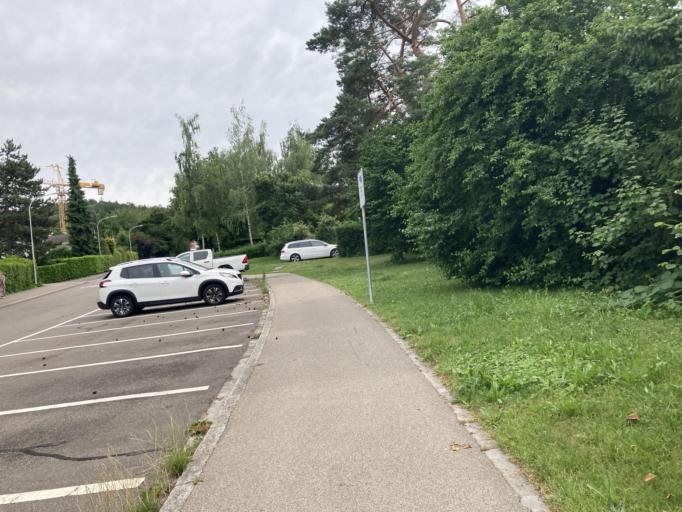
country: CH
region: Zurich
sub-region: Bezirk Horgen
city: Adliswil / Adliswil (Stadtkern)
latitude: 47.3082
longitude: 8.5283
